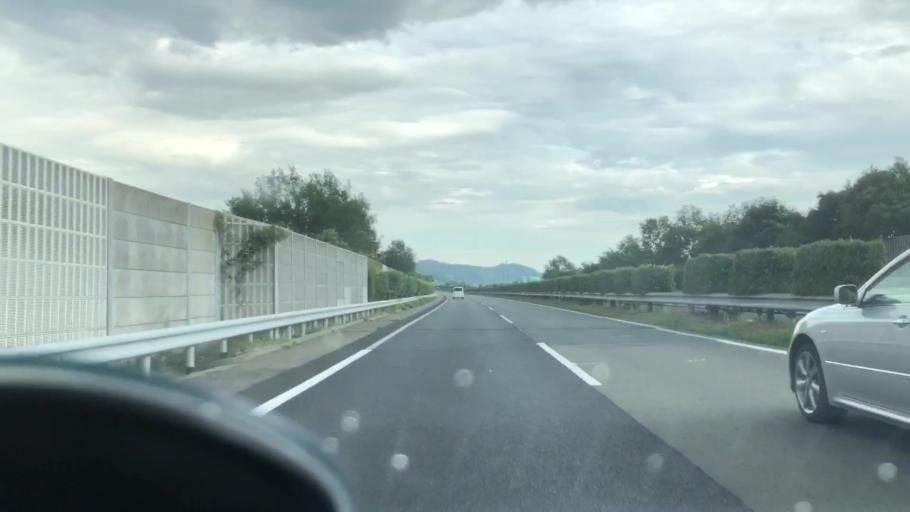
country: JP
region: Hyogo
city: Ono
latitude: 34.9426
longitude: 134.8138
